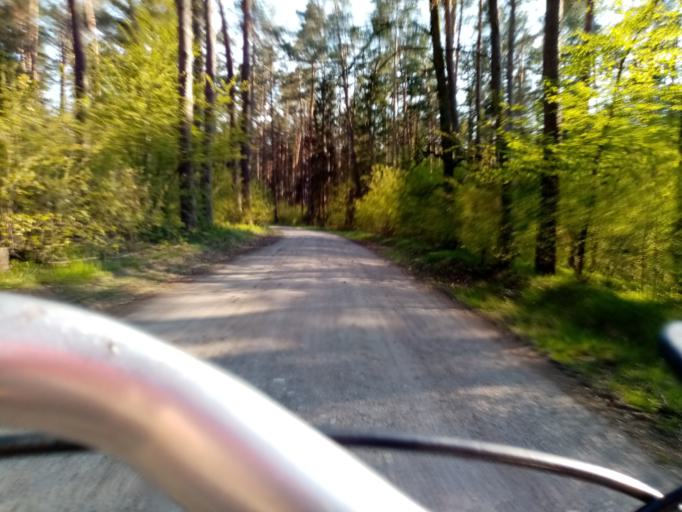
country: PL
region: Kujawsko-Pomorskie
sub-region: Powiat brodnicki
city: Gorzno
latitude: 53.1604
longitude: 19.7114
